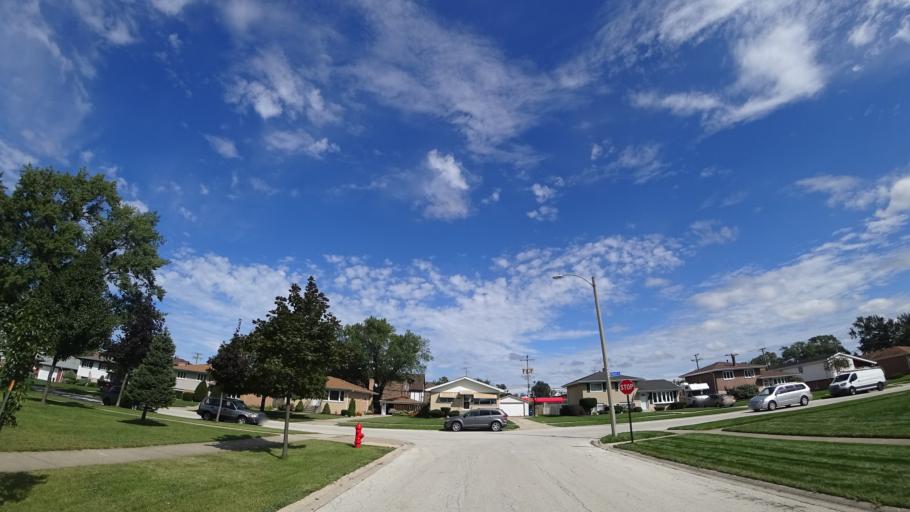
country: US
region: Illinois
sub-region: Cook County
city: Chicago Ridge
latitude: 41.6985
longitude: -87.7812
